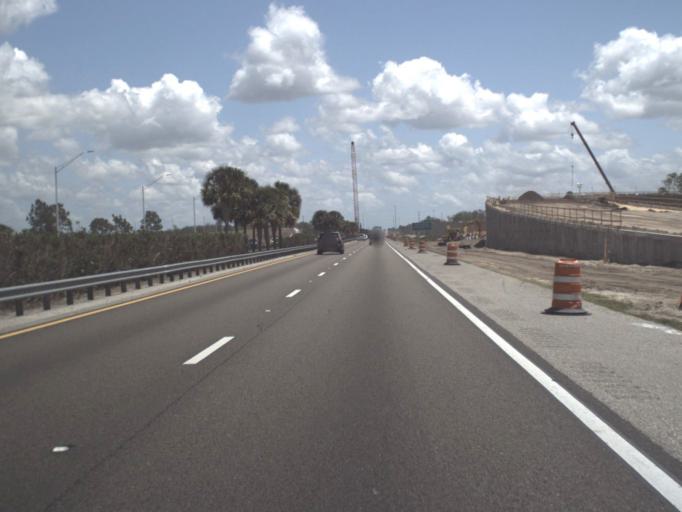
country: US
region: Florida
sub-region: Orange County
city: Wedgefield
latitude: 28.4516
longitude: -81.1767
